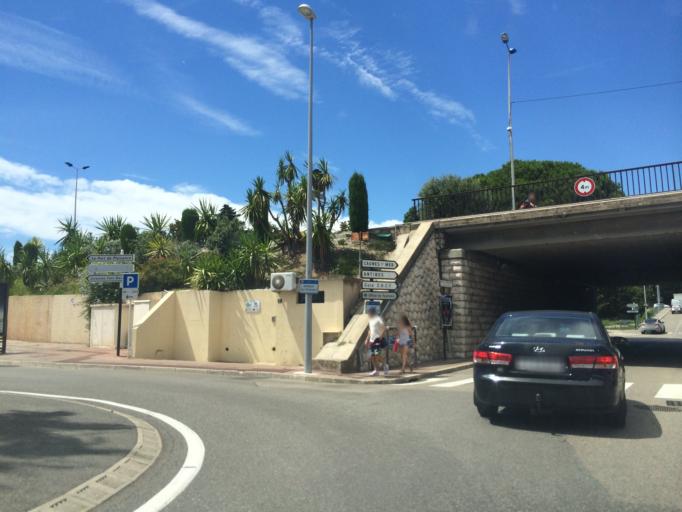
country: FR
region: Provence-Alpes-Cote d'Azur
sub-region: Departement des Alpes-Maritimes
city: Saint-Laurent-du-Var
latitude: 43.6590
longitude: 7.1904
